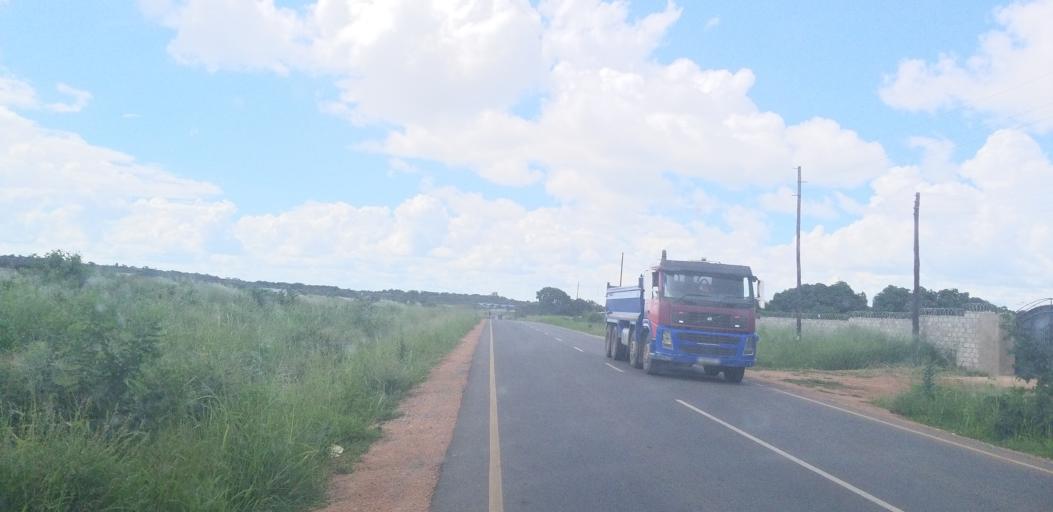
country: ZM
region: Lusaka
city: Lusaka
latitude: -15.3267
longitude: 28.3275
